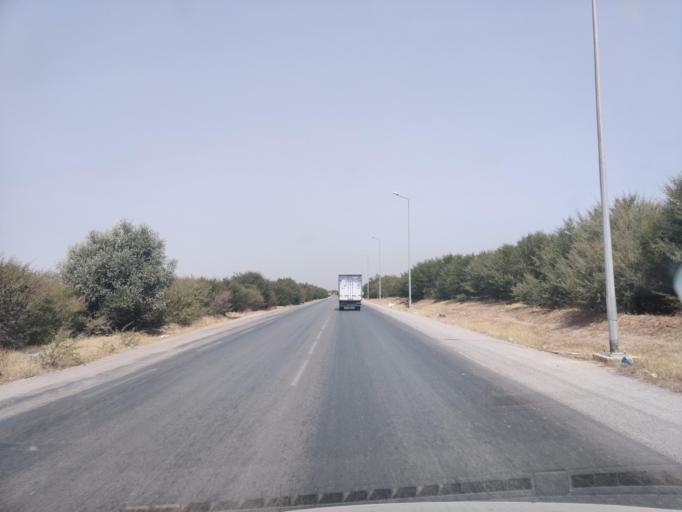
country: TN
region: Tunis
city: La Sebala du Mornag
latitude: 36.6673
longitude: 10.3247
